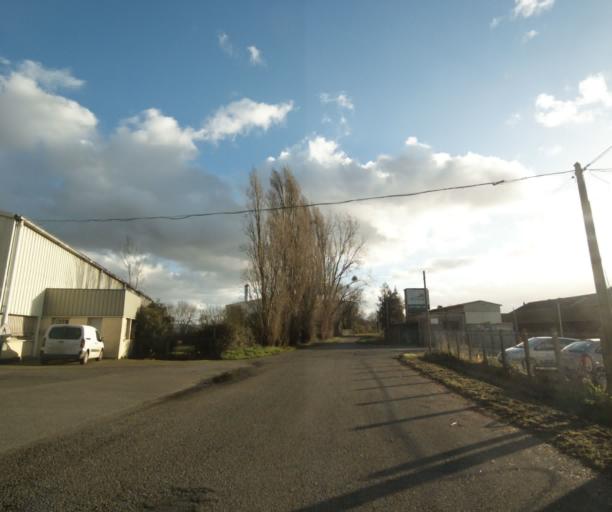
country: FR
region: Pays de la Loire
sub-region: Departement de la Sarthe
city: Allonnes
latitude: 47.9839
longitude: 0.1669
